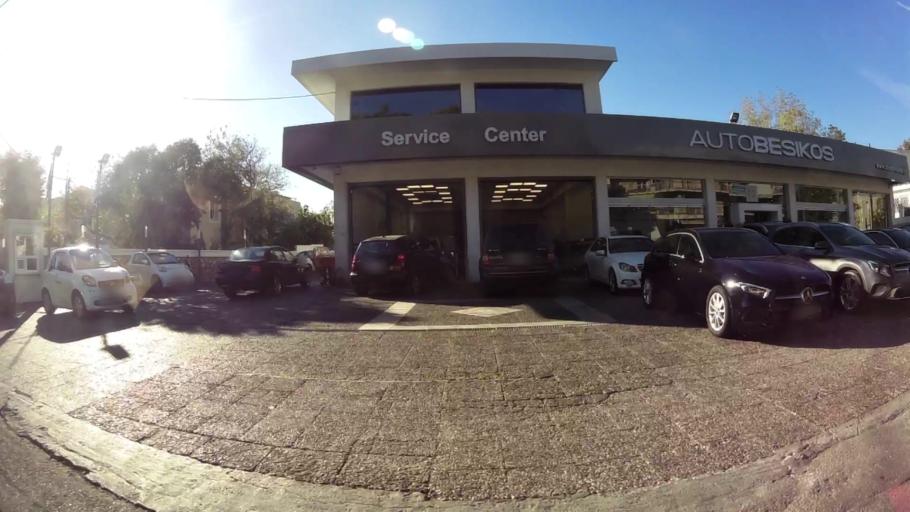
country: GR
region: Attica
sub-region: Nomarchia Athinas
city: Kifisia
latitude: 38.0804
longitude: 23.8143
